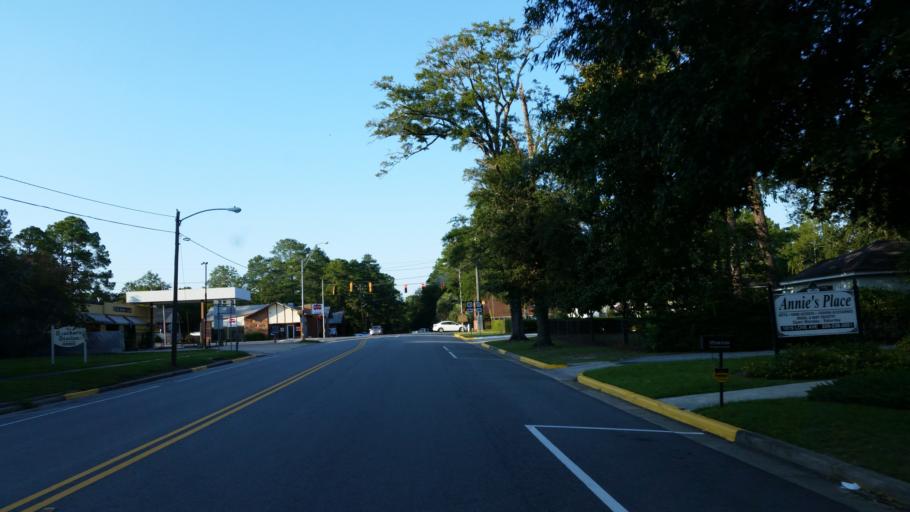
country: US
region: Georgia
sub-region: Tift County
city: Tifton
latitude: 31.4622
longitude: -83.5059
